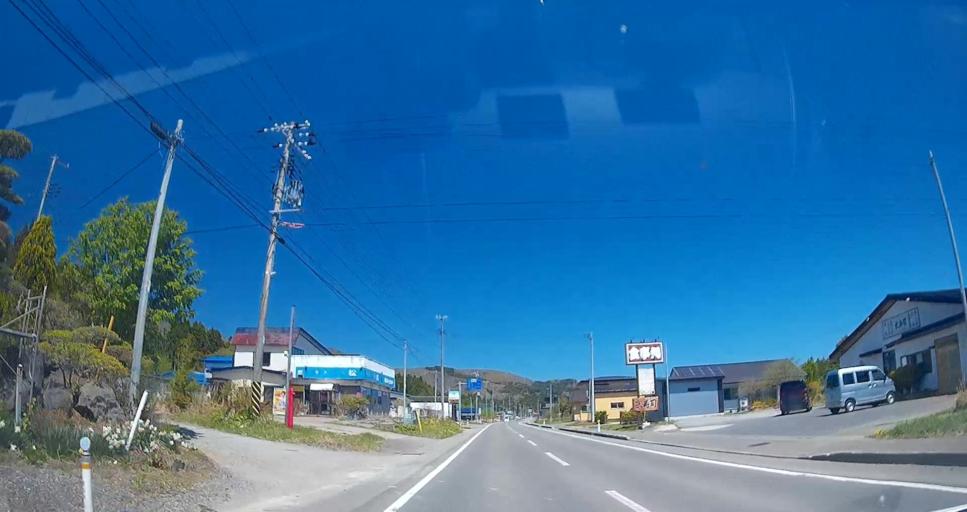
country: JP
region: Aomori
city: Mutsu
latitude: 41.0800
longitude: 141.3857
